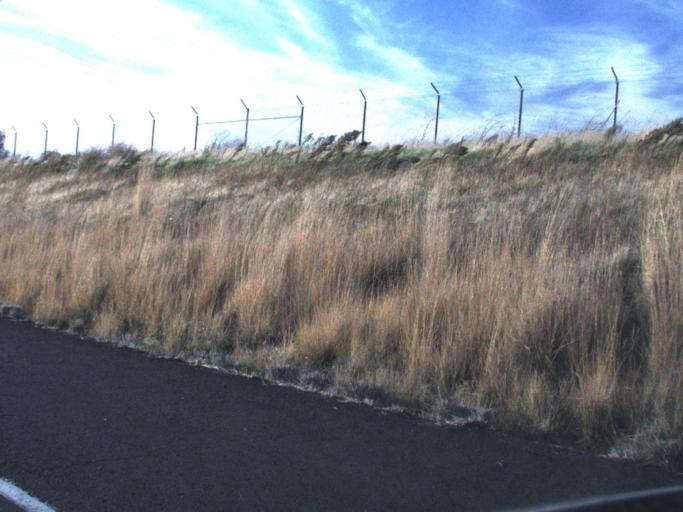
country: US
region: Washington
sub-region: Walla Walla County
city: Walla Walla East
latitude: 46.0825
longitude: -118.2969
